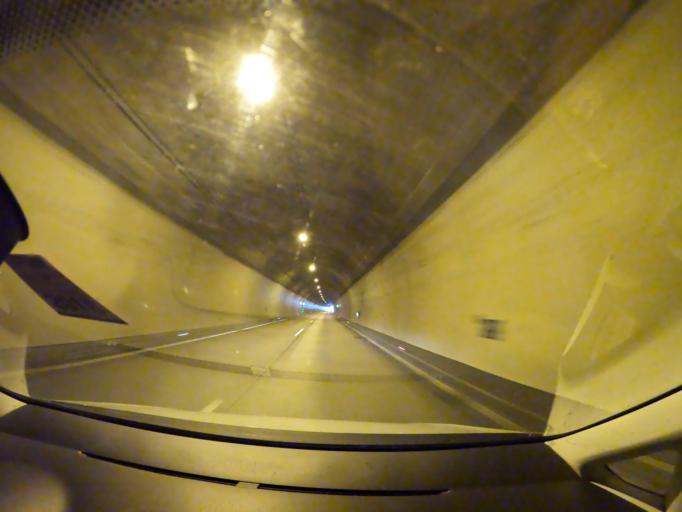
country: AT
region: Styria
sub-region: Politischer Bezirk Voitsberg
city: Pack
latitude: 46.9521
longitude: 15.0083
